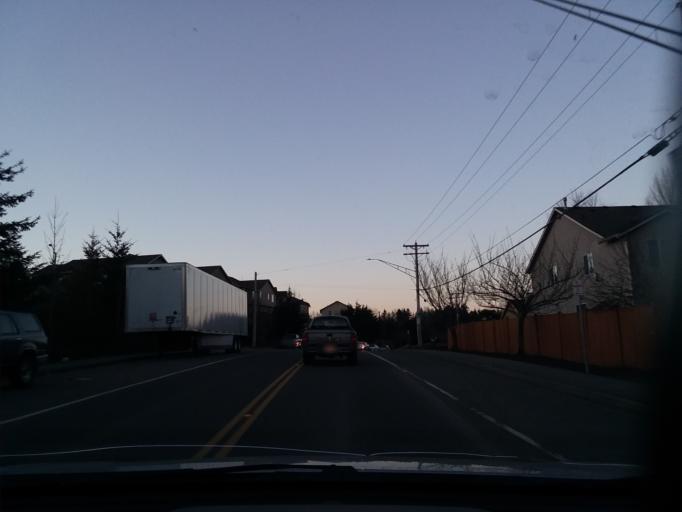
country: US
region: Washington
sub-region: Snohomish County
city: Martha Lake
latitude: 47.8666
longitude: -122.2682
